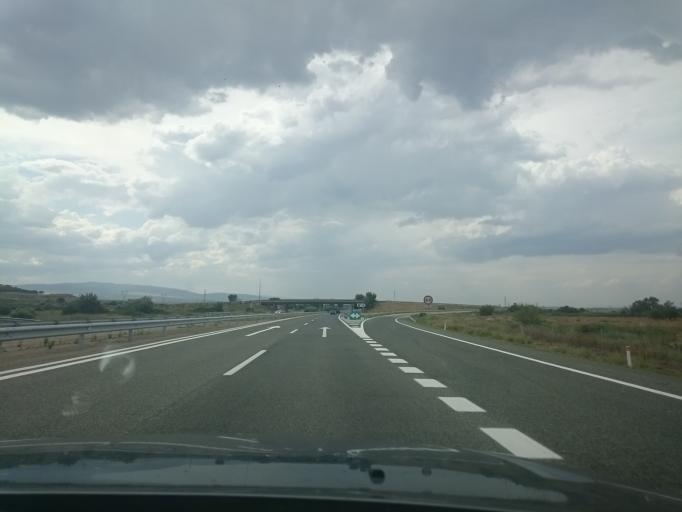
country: ES
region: Navarre
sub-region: Provincia de Navarra
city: Corella
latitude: 42.1329
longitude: -1.7671
